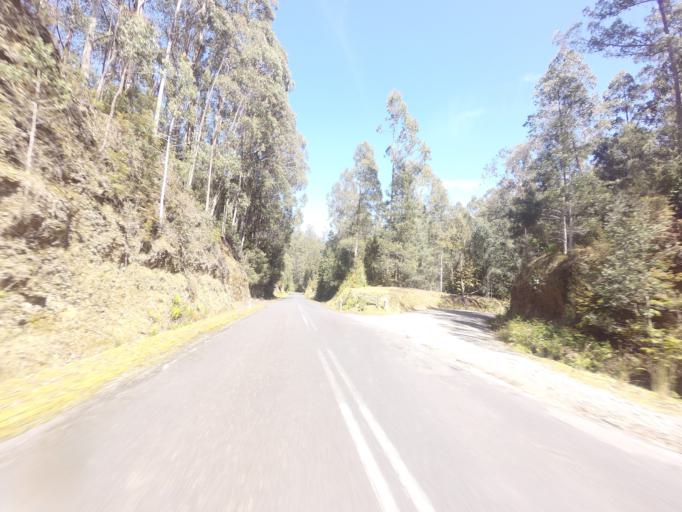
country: AU
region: Tasmania
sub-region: Huon Valley
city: Geeveston
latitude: -42.8173
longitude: 146.3451
